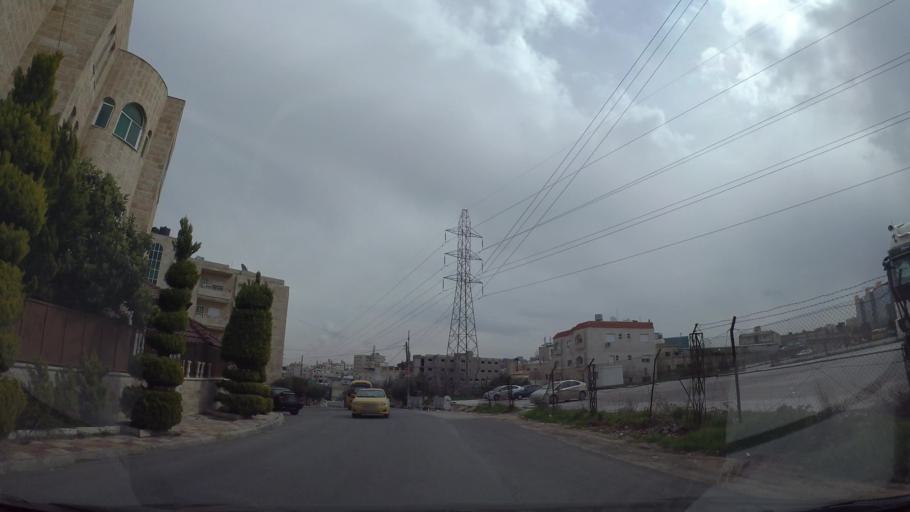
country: JO
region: Amman
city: Amman
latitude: 31.9928
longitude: 35.9434
